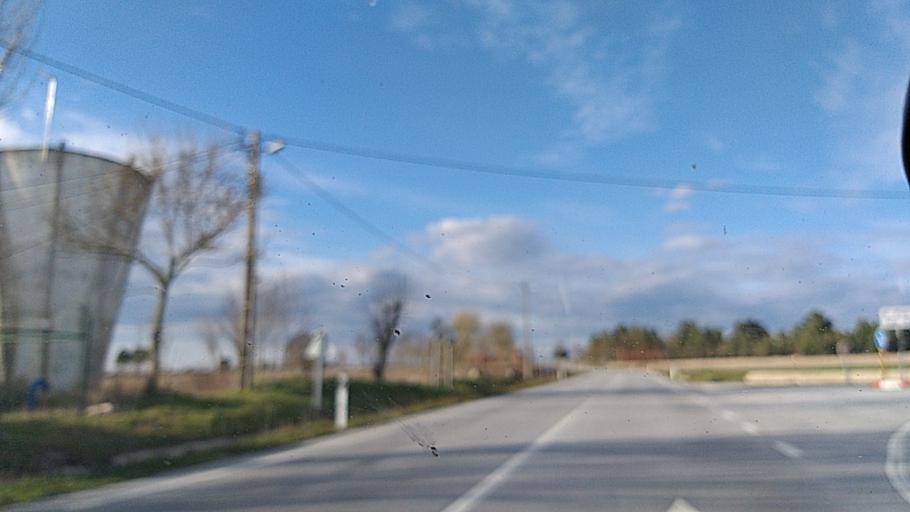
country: ES
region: Castille and Leon
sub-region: Provincia de Salamanca
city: Aldea del Obispo
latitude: 40.6605
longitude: -6.8571
